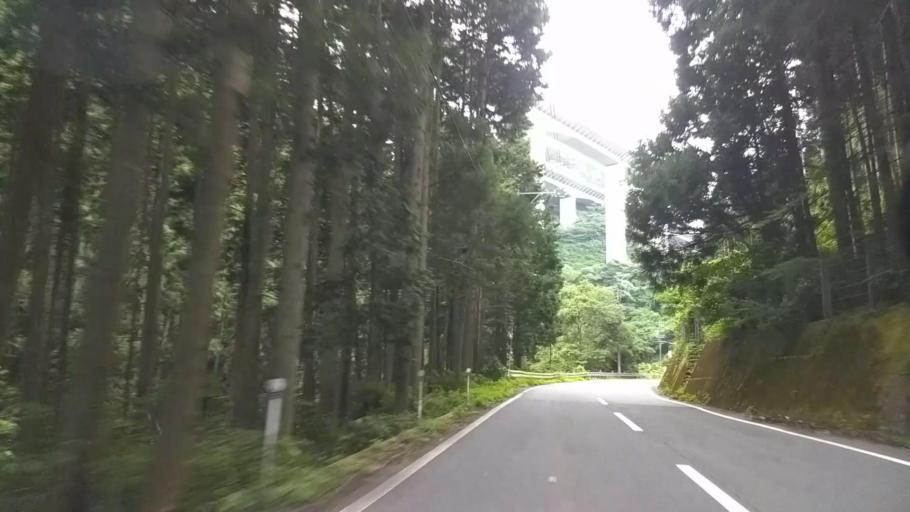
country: JP
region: Shizuoka
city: Fujinomiya
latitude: 35.1568
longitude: 138.5398
